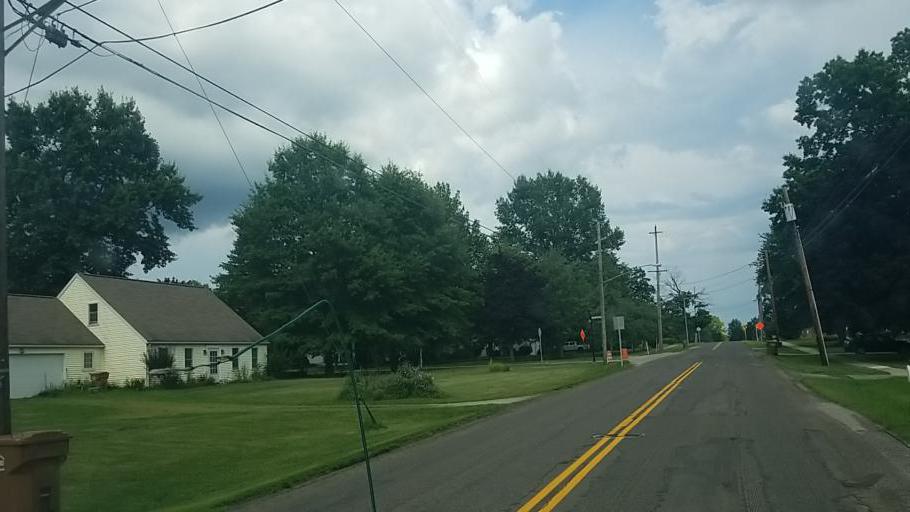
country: US
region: Ohio
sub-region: Medina County
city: Westfield Center
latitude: 41.0268
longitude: -81.9388
